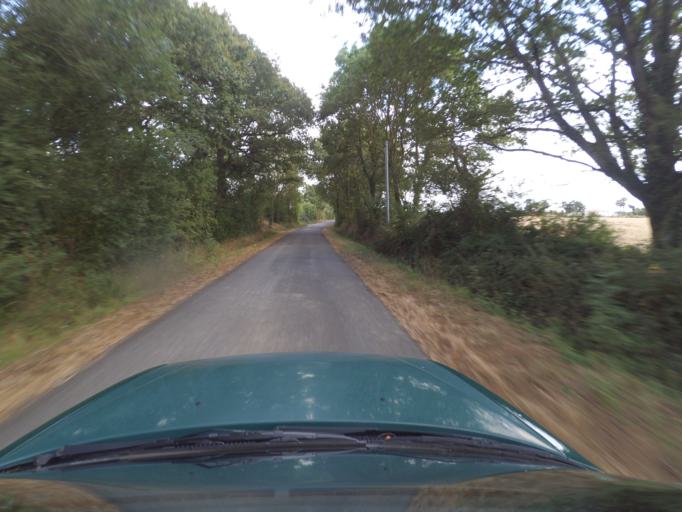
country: FR
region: Pays de la Loire
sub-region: Departement de la Loire-Atlantique
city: Vieillevigne
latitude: 46.9827
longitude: -1.4535
